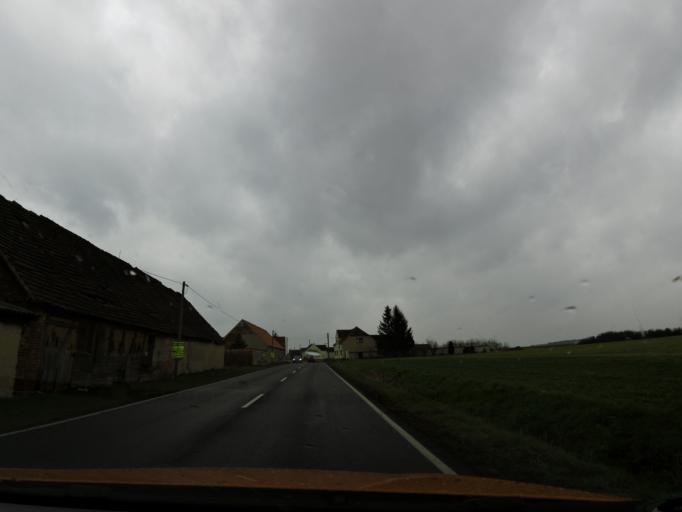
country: DE
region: Brandenburg
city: Ziesar
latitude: 52.2787
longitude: 12.2384
